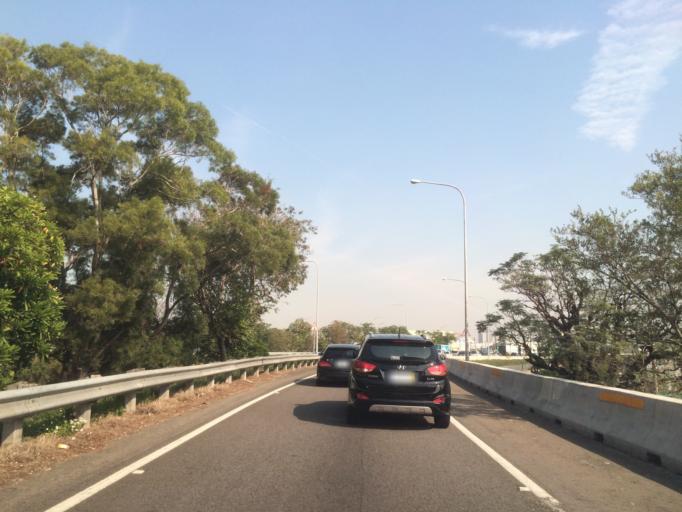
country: TW
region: Taiwan
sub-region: Taichung City
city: Taichung
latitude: 24.2055
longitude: 120.6583
